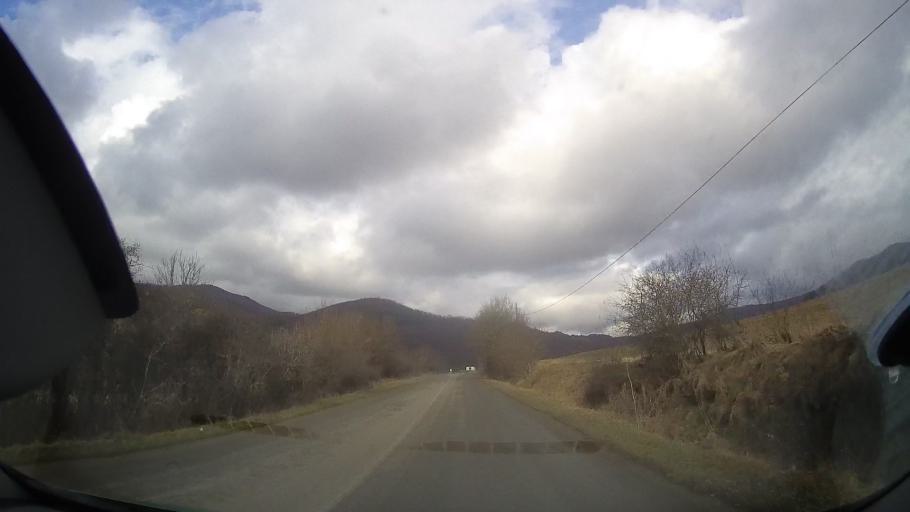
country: RO
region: Alba
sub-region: Comuna Rimetea
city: Rimetea
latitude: 46.4612
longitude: 23.5720
